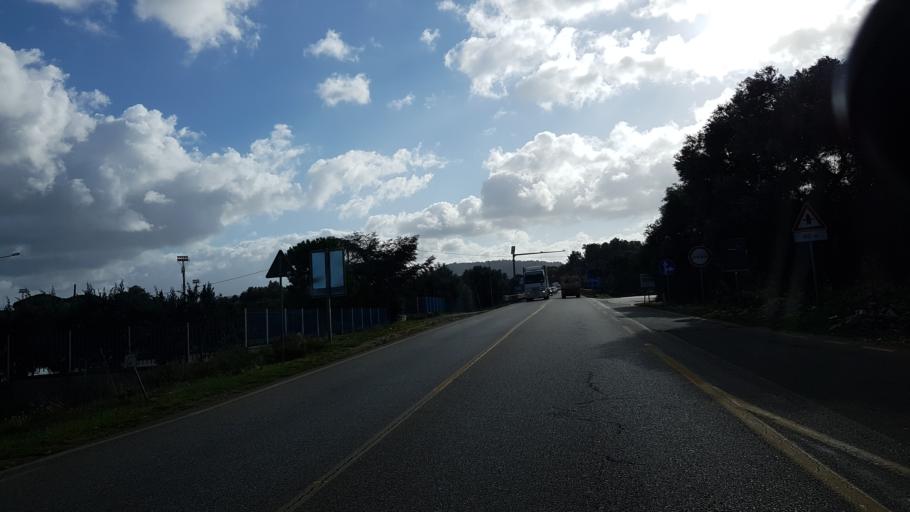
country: IT
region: Apulia
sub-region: Provincia di Brindisi
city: Fasano
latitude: 40.8322
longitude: 17.3502
